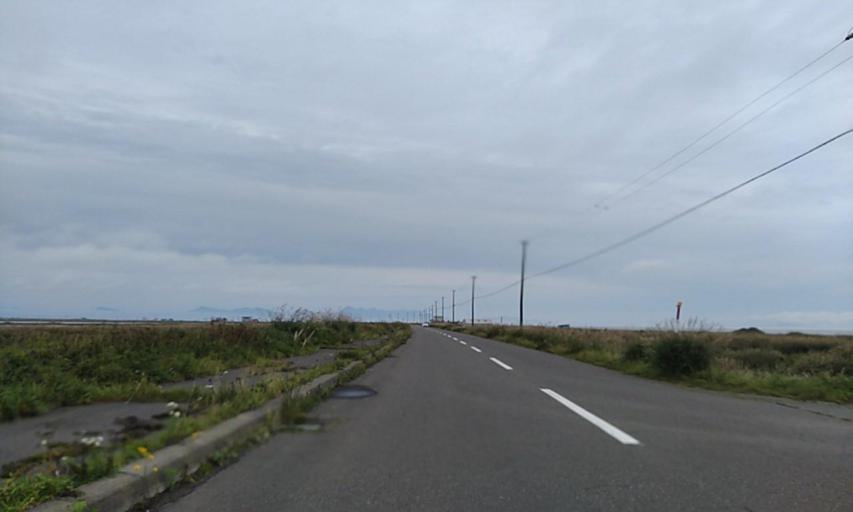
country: JP
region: Hokkaido
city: Shibetsu
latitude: 43.5790
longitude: 145.3435
